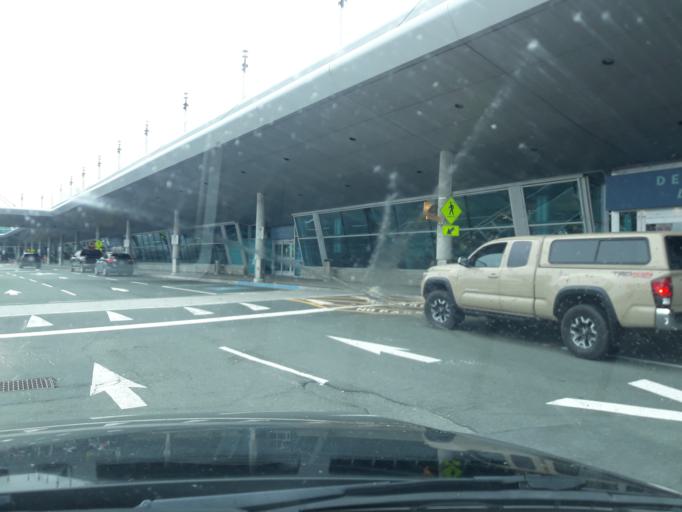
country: CA
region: Newfoundland and Labrador
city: Torbay
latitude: 47.6126
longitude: -52.7426
